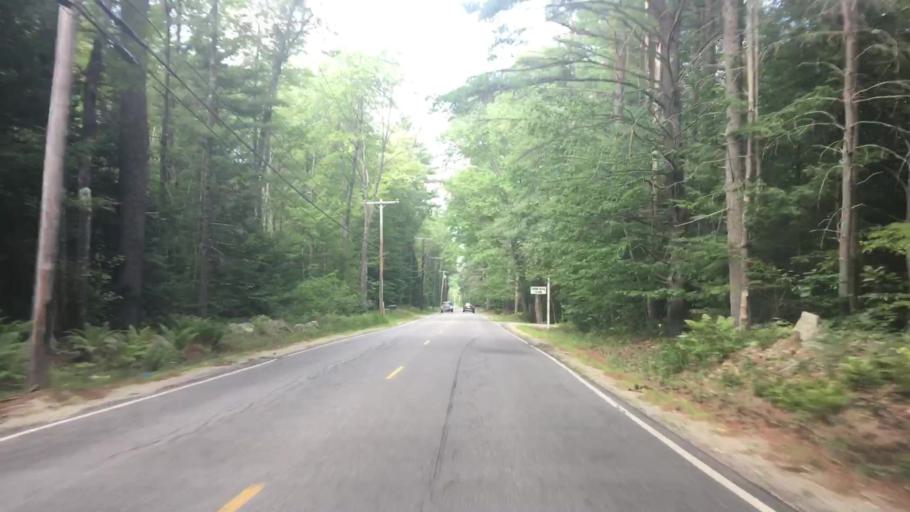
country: US
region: Maine
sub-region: Oxford County
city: Oxford
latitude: 44.1160
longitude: -70.5059
